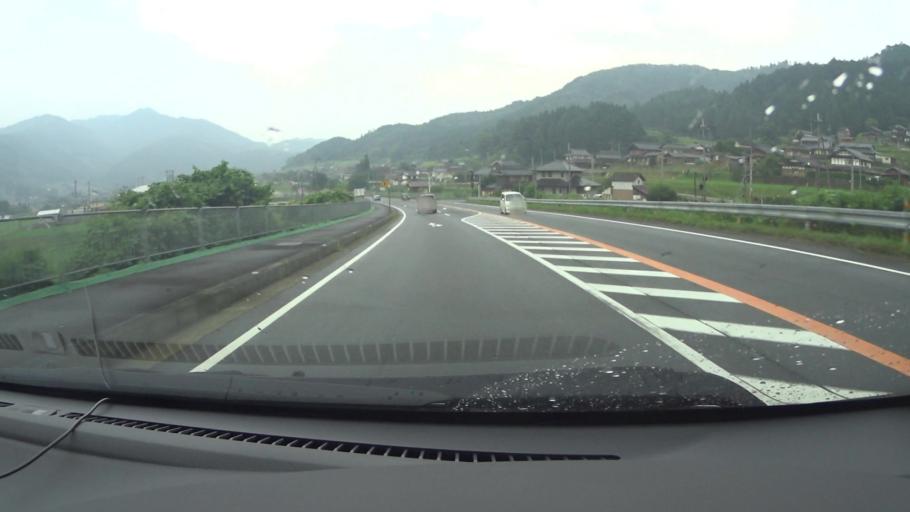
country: JP
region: Kyoto
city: Ayabe
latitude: 35.2660
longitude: 135.3800
